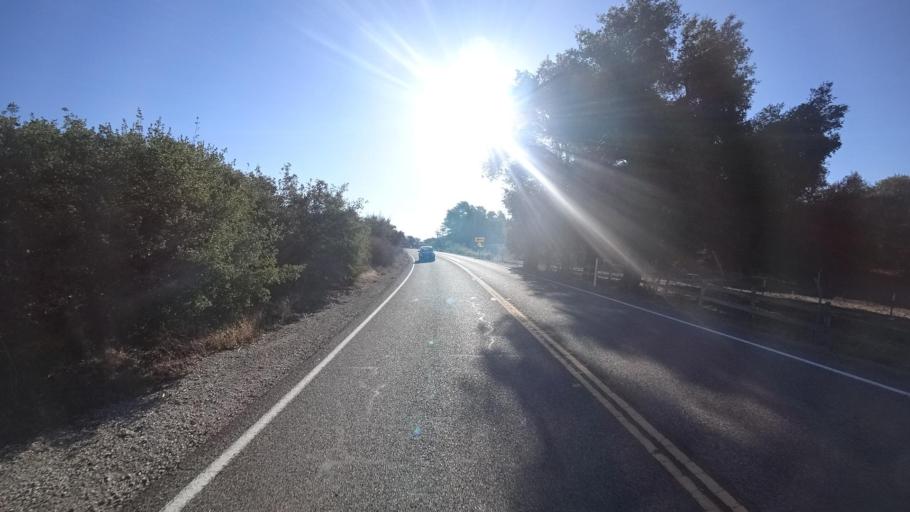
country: MX
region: Baja California
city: Tecate
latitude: 32.5998
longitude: -116.5863
